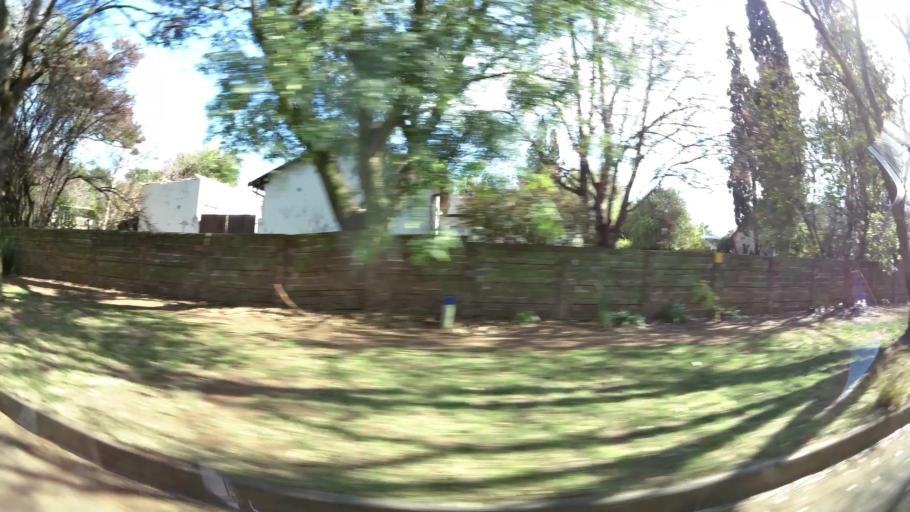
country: ZA
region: Gauteng
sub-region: Ekurhuleni Metropolitan Municipality
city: Benoni
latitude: -26.1436
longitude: 28.3466
